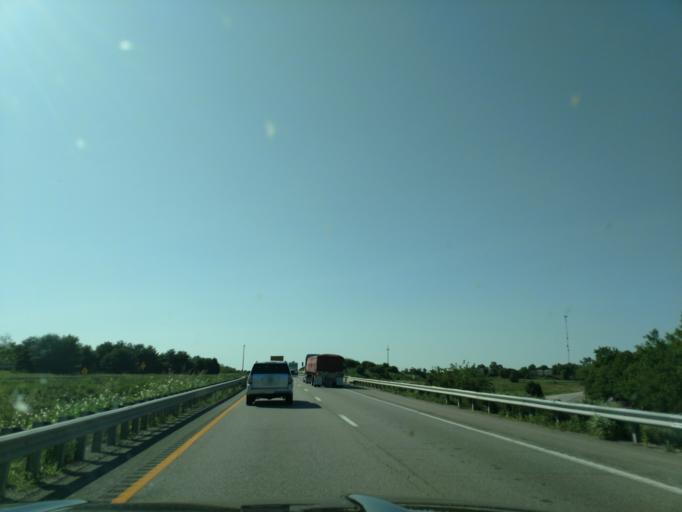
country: US
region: Missouri
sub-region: Andrew County
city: Savannah
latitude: 39.8858
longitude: -94.8554
